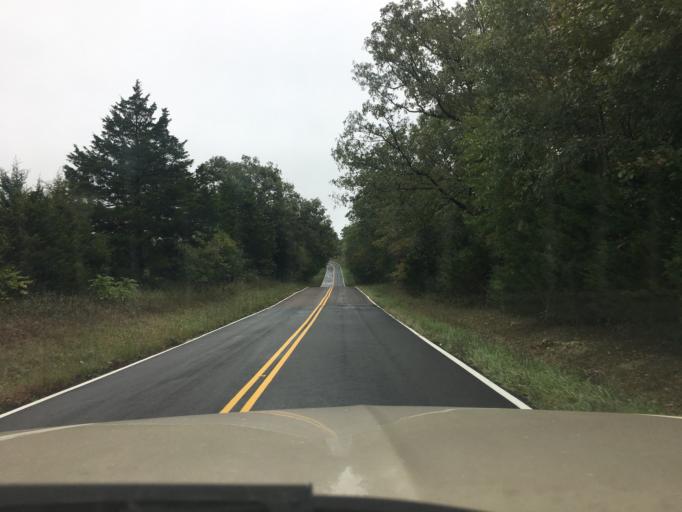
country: US
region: Missouri
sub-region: Crawford County
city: Cuba
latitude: 38.1764
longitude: -91.4929
